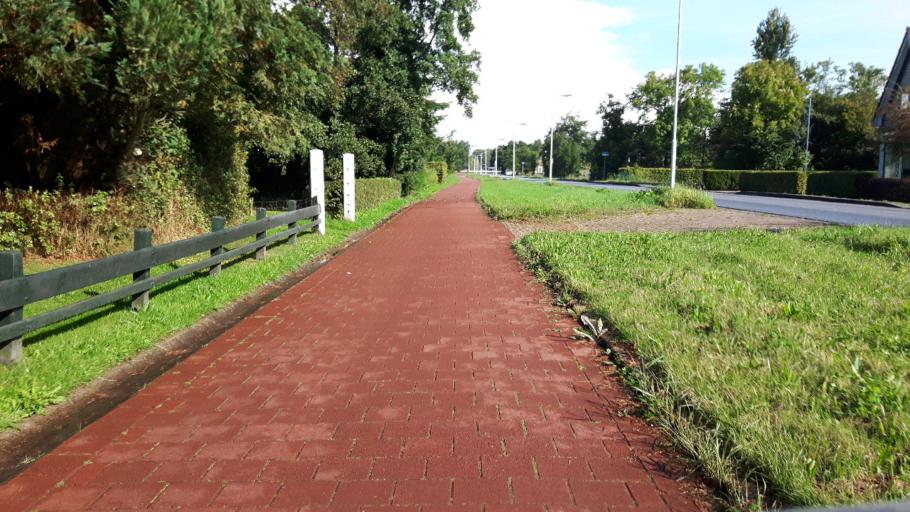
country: NL
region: Friesland
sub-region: Gemeente Smallingerland
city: Drachten
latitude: 53.0888
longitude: 6.0996
